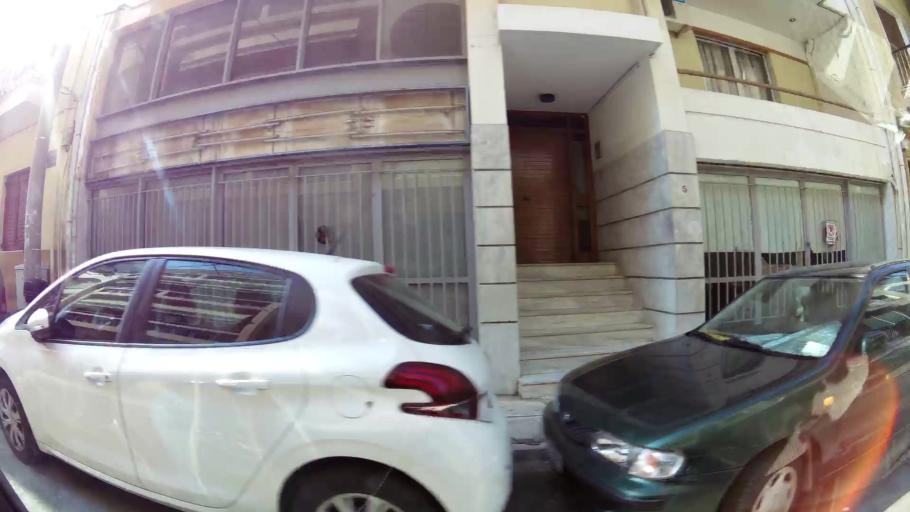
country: GR
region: Attica
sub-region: Nomarchia Athinas
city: Galatsi
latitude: 38.0146
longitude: 23.7489
